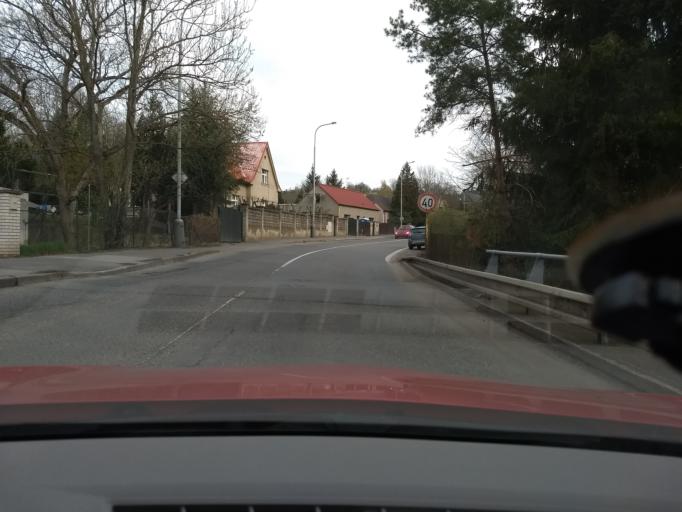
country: CZ
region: Central Bohemia
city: Horomerice
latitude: 50.1060
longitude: 14.3534
